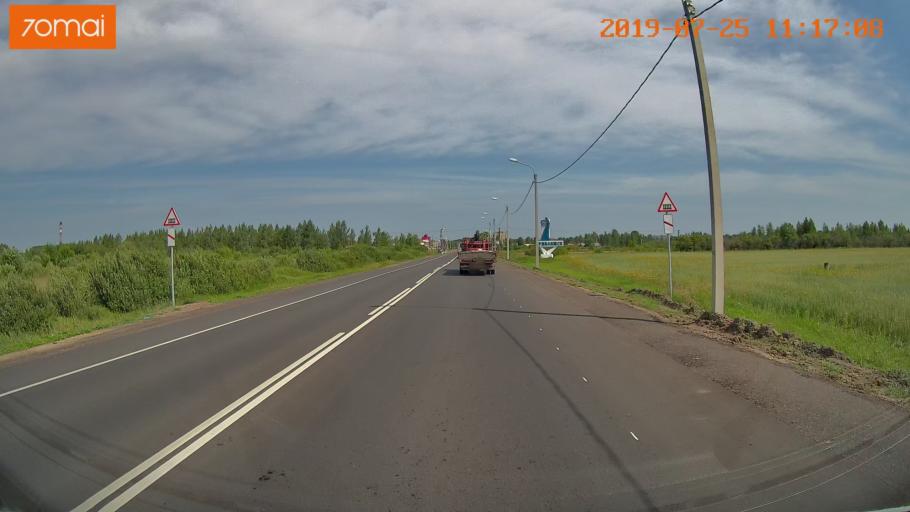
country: RU
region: Ivanovo
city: Privolzhsk
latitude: 57.3642
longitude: 41.2695
